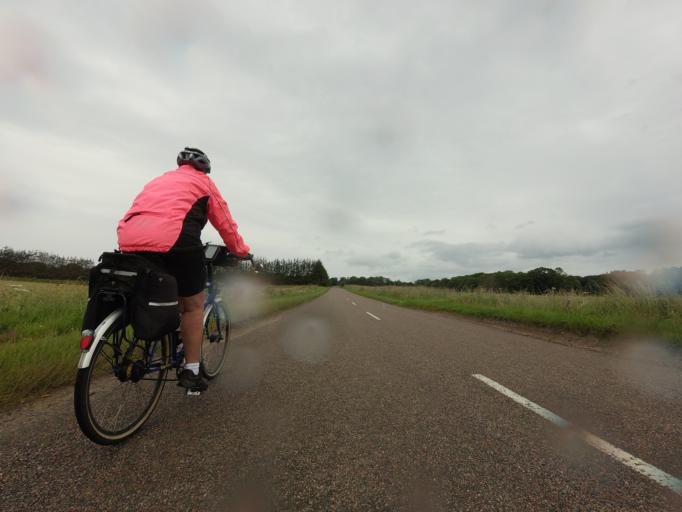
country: GB
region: Scotland
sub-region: Moray
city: Cullen
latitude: 57.6789
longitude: -2.8132
